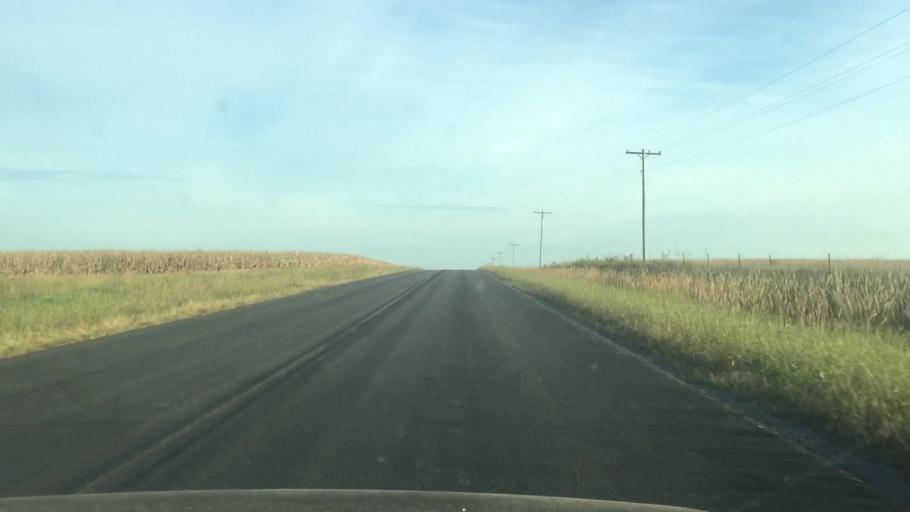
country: US
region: Kansas
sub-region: Marshall County
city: Marysville
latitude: 39.9181
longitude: -96.6009
